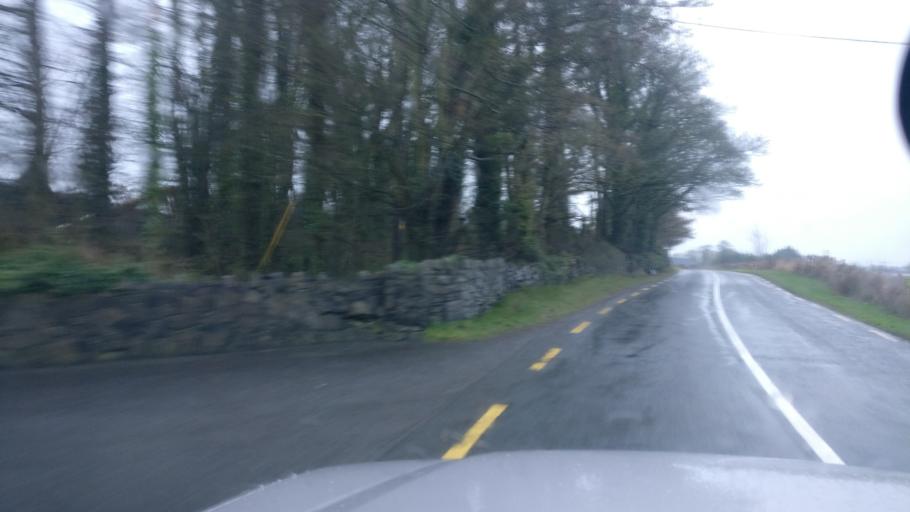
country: IE
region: Connaught
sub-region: County Galway
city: Ballinasloe
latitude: 53.2553
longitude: -8.1799
